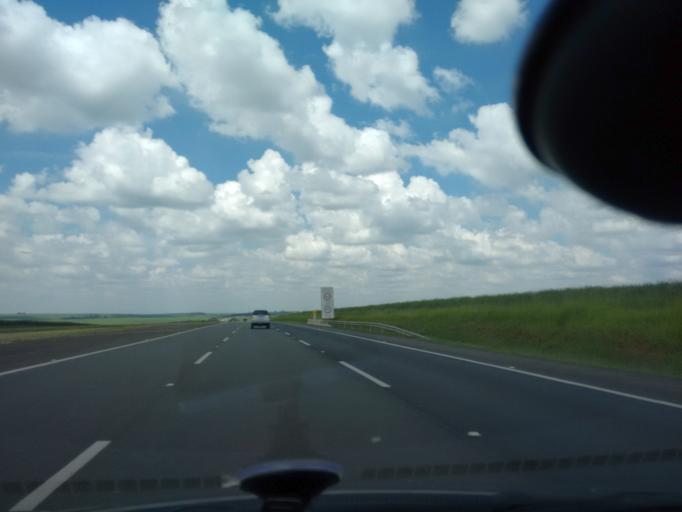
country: BR
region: Sao Paulo
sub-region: Santa Barbara D'Oeste
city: Santa Barbara d'Oeste
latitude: -22.7888
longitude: -47.4233
